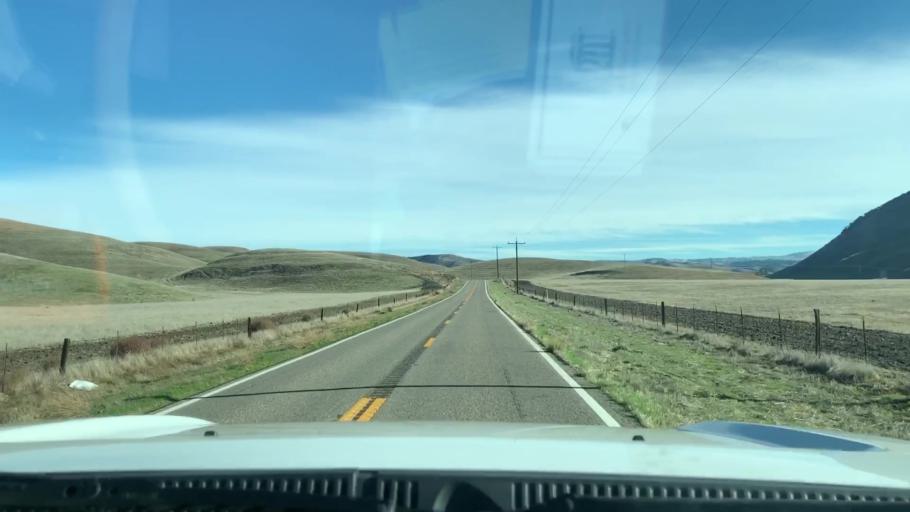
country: US
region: California
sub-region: Monterey County
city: King City
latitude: 36.1566
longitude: -120.9100
